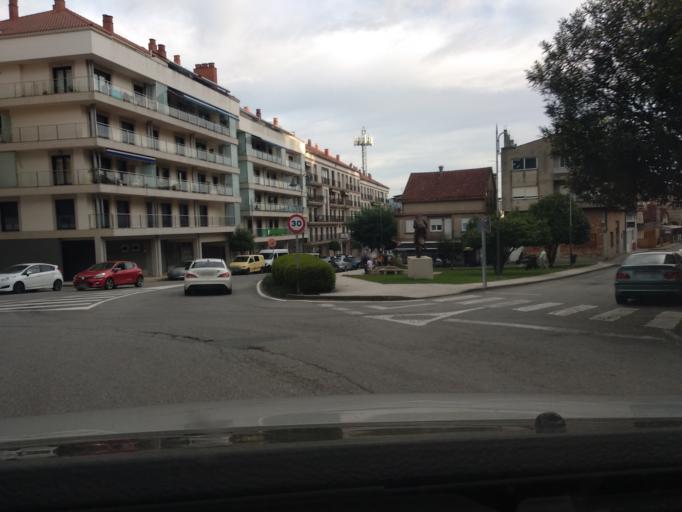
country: ES
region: Galicia
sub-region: Provincia de Pontevedra
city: Moana
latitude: 42.2889
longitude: -8.7359
